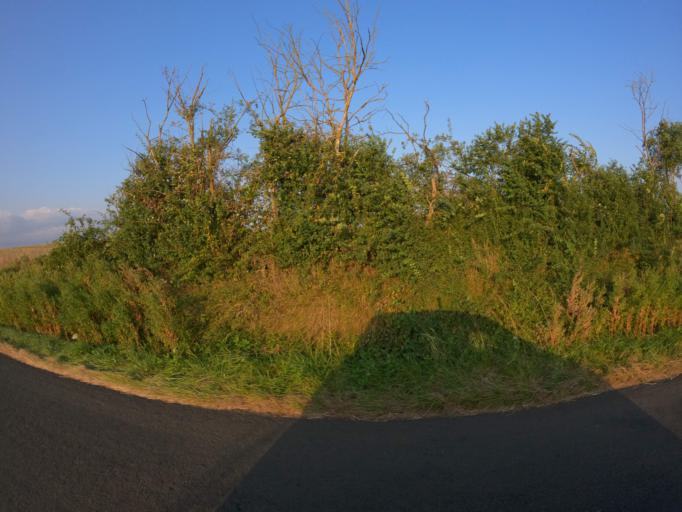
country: FR
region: Pays de la Loire
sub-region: Departement de la Sarthe
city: Brulon
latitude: 47.9373
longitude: -0.2248
